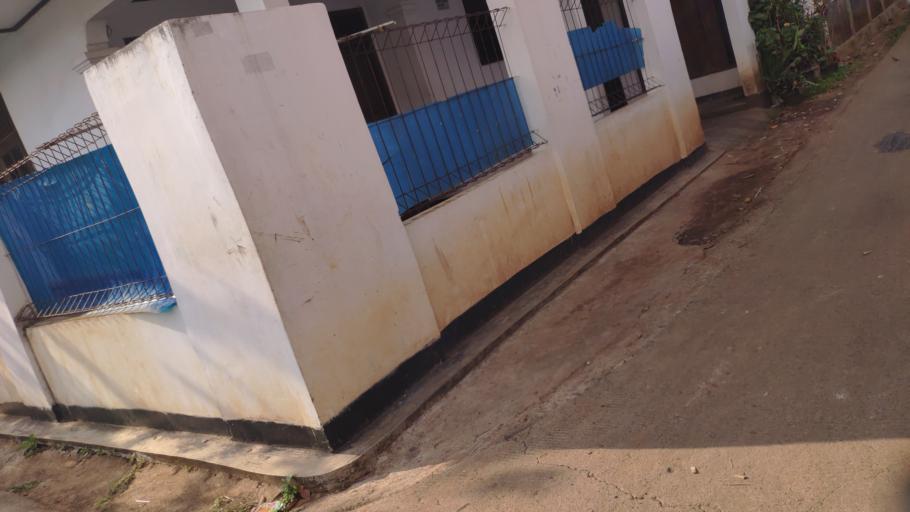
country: ID
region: West Java
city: Pamulang
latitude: -6.2991
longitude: 106.8018
